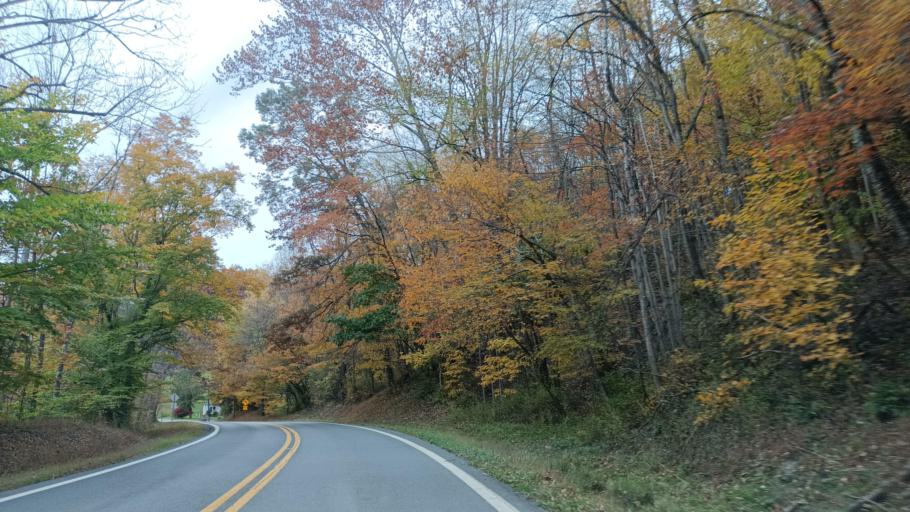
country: US
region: West Virginia
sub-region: Taylor County
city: Grafton
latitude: 39.3365
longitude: -79.9024
